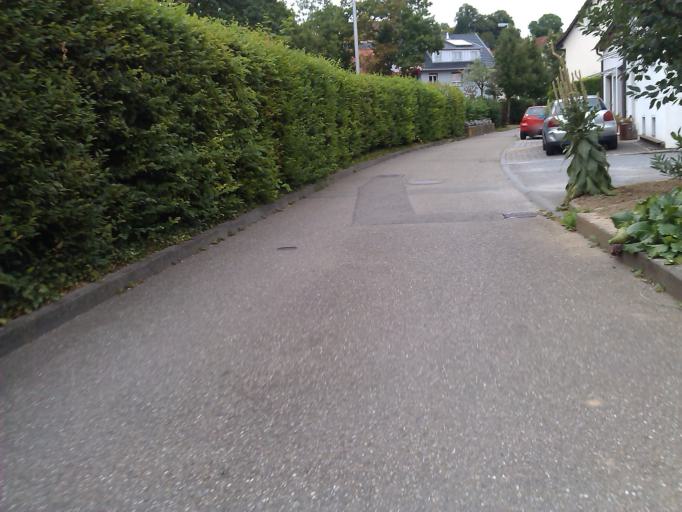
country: DE
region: Baden-Wuerttemberg
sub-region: Regierungsbezirk Stuttgart
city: Talheim
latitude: 49.0845
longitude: 9.1949
